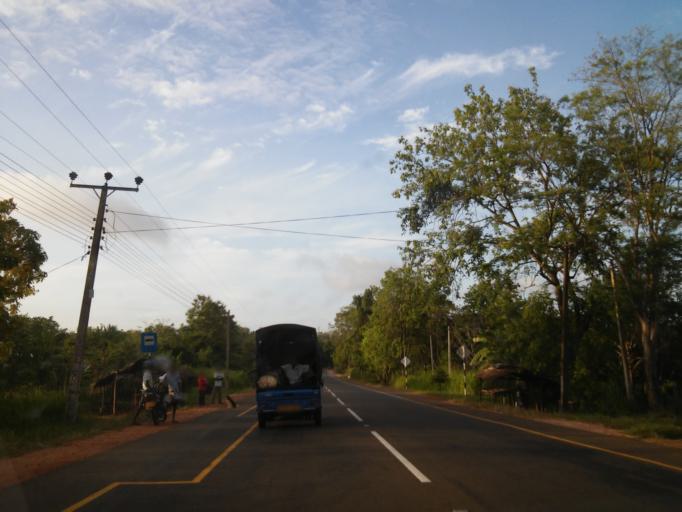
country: LK
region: North Central
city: Anuradhapura
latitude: 8.1644
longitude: 80.5369
